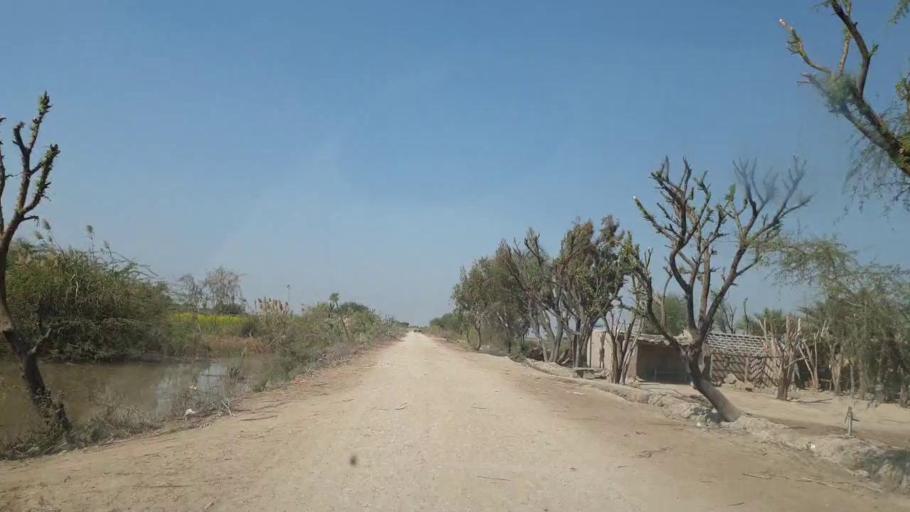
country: PK
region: Sindh
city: Mirpur Khas
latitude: 25.7309
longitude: 69.0664
